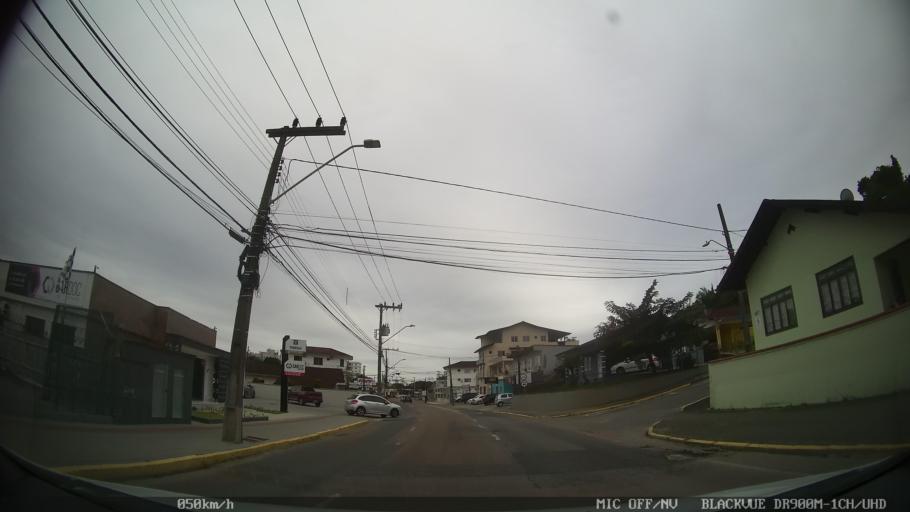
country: BR
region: Santa Catarina
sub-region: Joinville
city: Joinville
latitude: -26.2791
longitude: -48.8363
